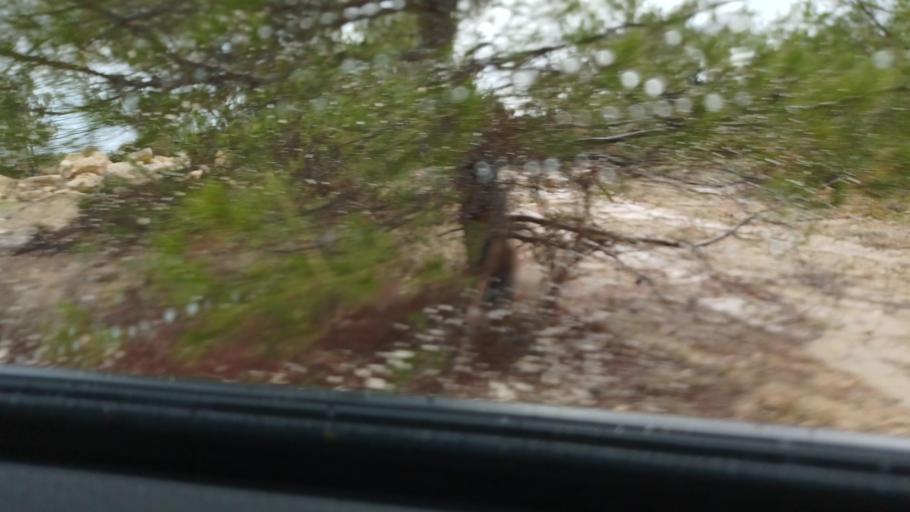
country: CY
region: Limassol
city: Sotira
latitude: 34.7442
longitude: 32.8551
